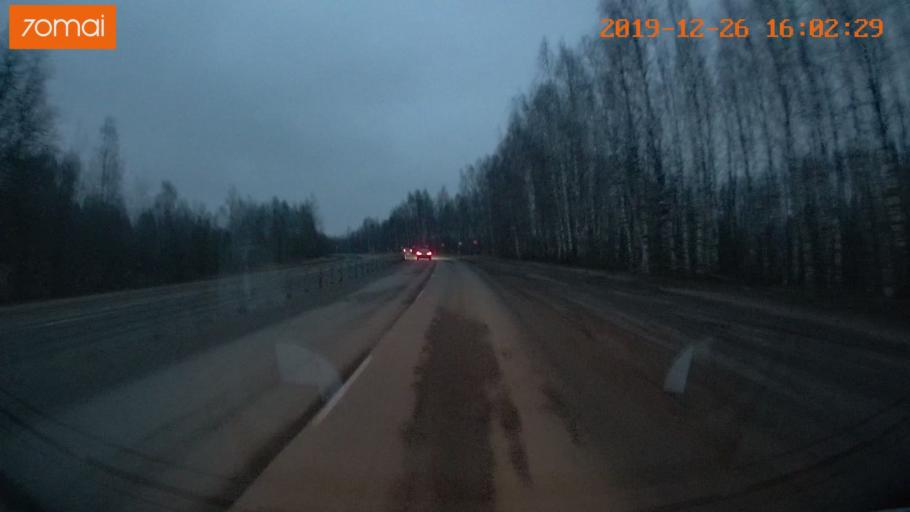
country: RU
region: Jaroslavl
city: Rybinsk
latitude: 58.0114
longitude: 38.8356
